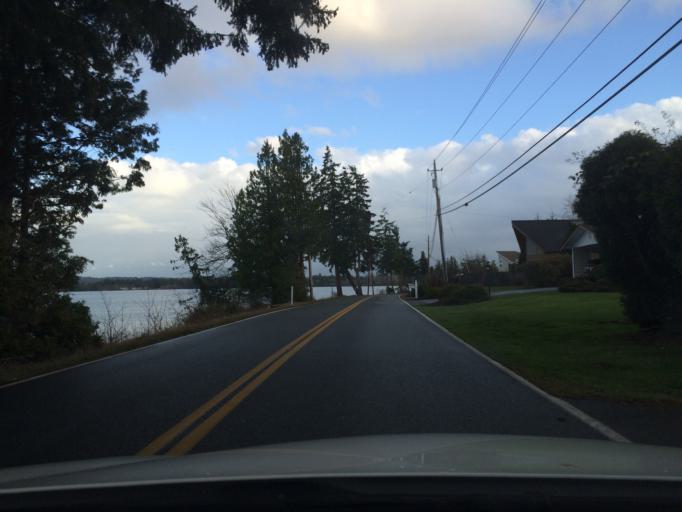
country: US
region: Washington
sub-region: Whatcom County
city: Blaine
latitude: 48.9610
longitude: -122.7592
